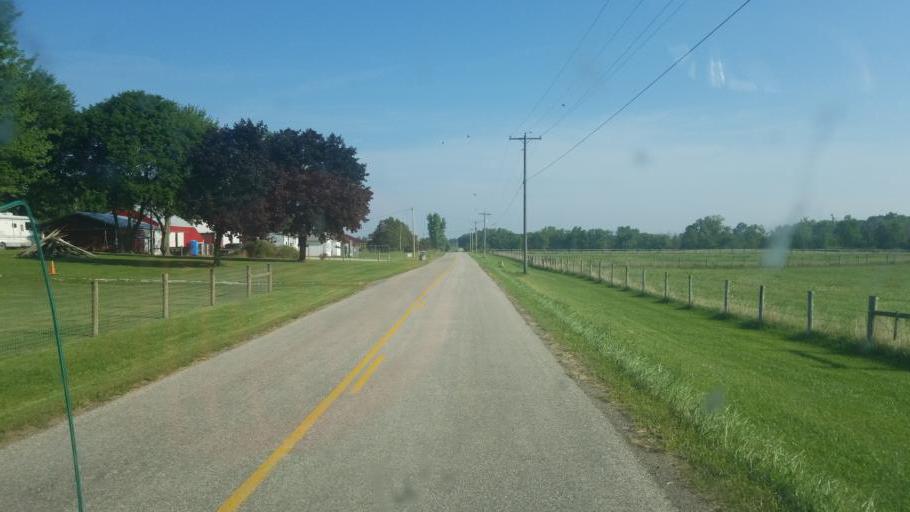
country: US
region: Ohio
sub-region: Huron County
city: New London
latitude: 41.0189
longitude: -82.3538
